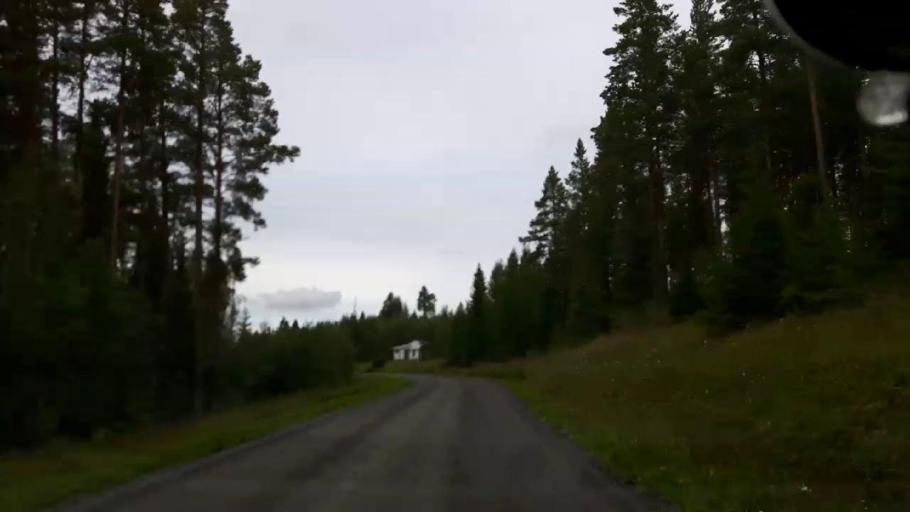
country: SE
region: Jaemtland
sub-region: Krokoms Kommun
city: Krokom
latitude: 63.3041
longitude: 14.3455
